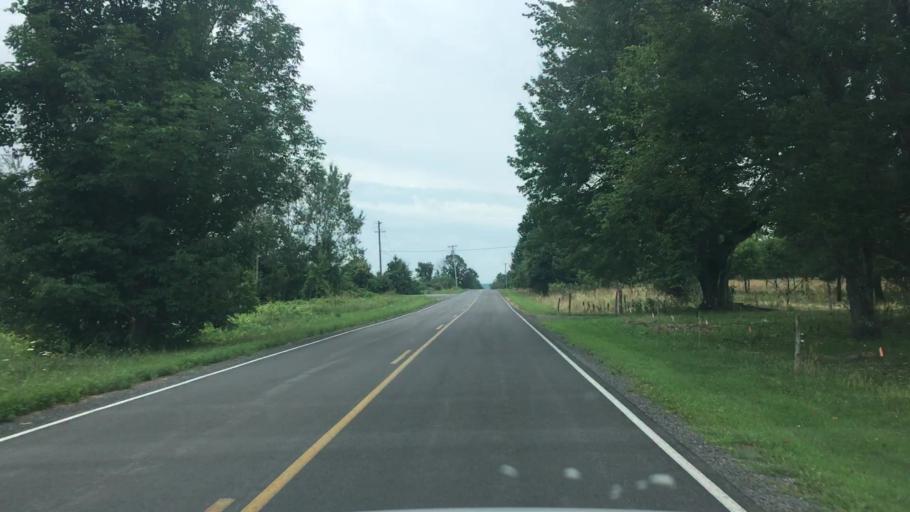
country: US
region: New York
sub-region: Clinton County
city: Peru
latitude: 44.6033
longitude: -73.6288
